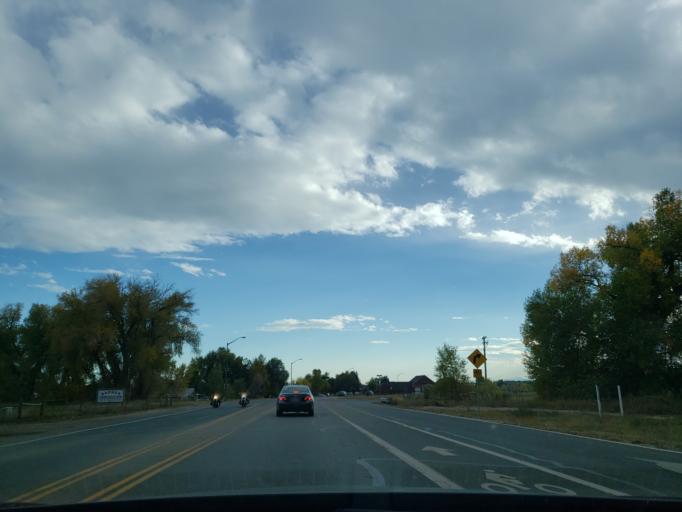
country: US
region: Colorado
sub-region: Larimer County
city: Fort Collins
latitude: 40.5887
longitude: -105.0296
